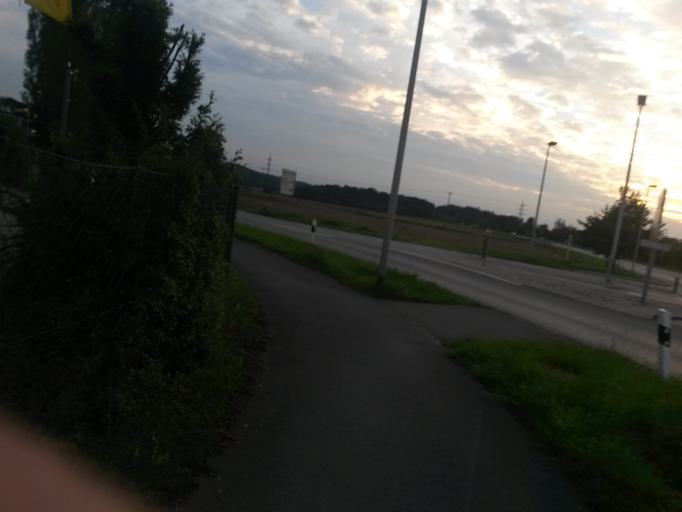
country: DE
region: Bavaria
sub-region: Regierungsbezirk Mittelfranken
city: Zirndorf
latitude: 49.4319
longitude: 10.9352
